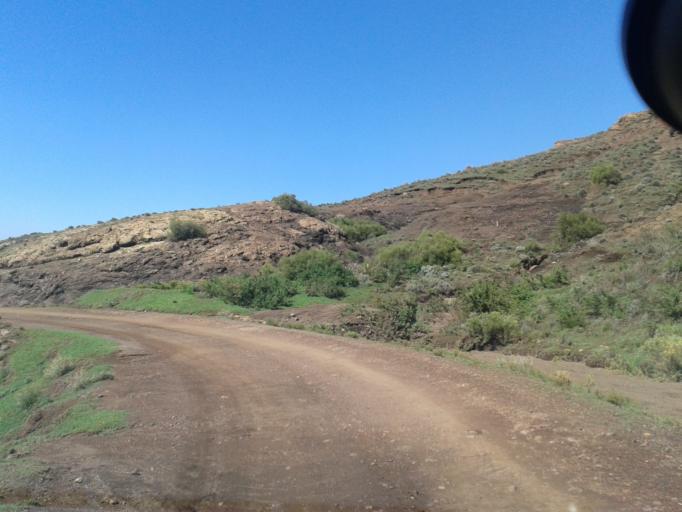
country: LS
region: Maseru
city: Nako
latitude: -29.8398
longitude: 27.5678
